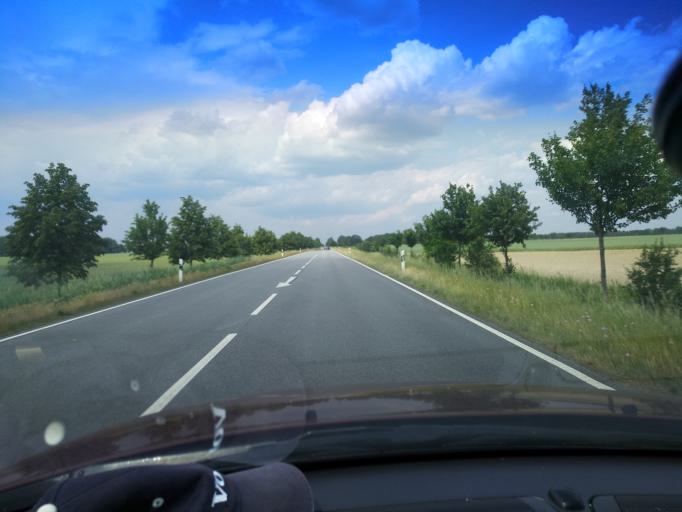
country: DE
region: Saxony
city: Kodersdorf
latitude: 51.2590
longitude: 14.8668
